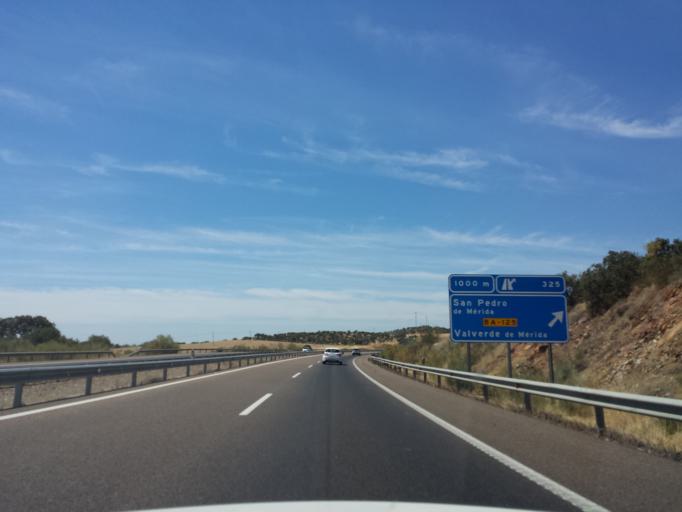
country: ES
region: Extremadura
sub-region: Provincia de Badajoz
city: San Pedro de Merida
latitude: 38.9528
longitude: -6.1650
